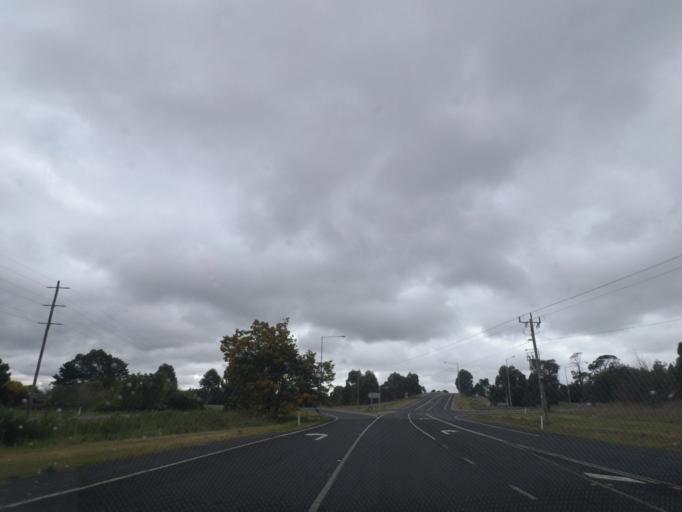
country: AU
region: Victoria
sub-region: Hume
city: Sunbury
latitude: -37.3231
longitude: 144.5240
